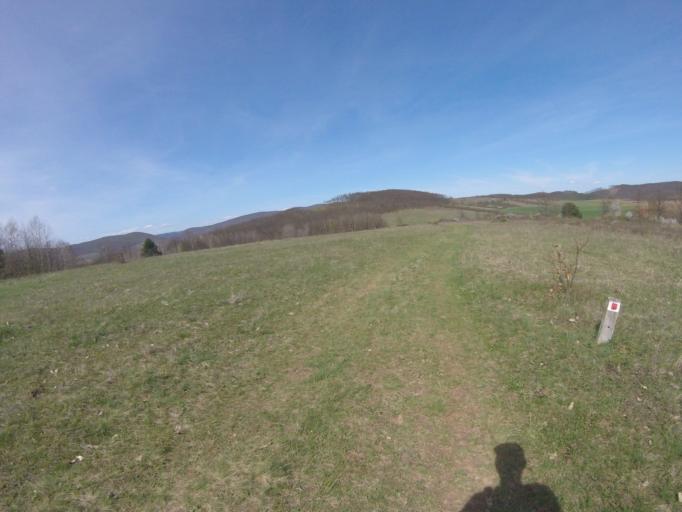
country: HU
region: Borsod-Abauj-Zemplen
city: Szendro
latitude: 48.4265
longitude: 20.7546
